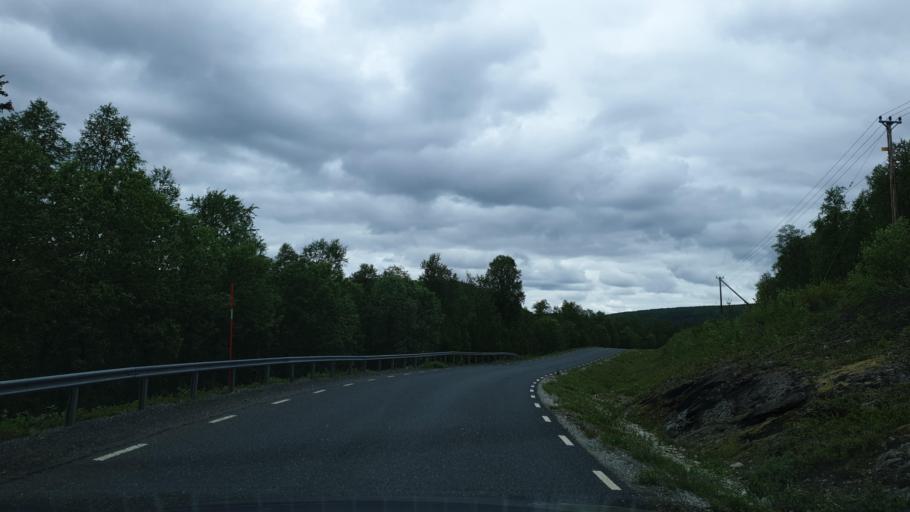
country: SE
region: Vaesterbotten
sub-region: Vilhelmina Kommun
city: Sjoberg
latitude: 65.2964
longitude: 15.2893
